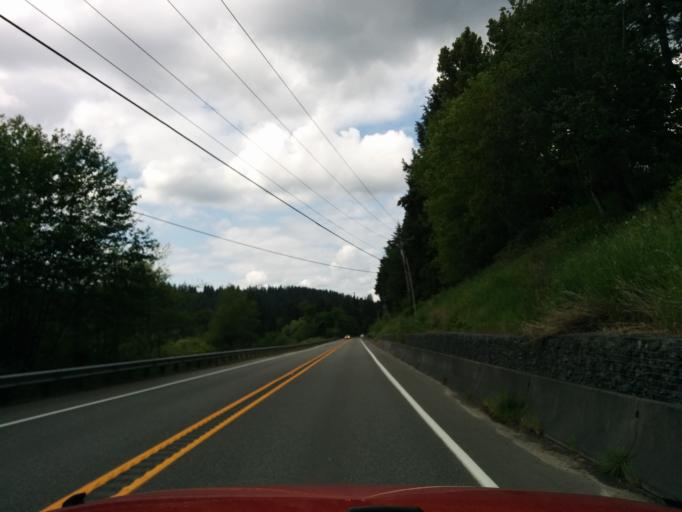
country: US
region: Washington
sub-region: King County
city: Ames Lake
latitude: 47.5909
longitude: -121.9570
